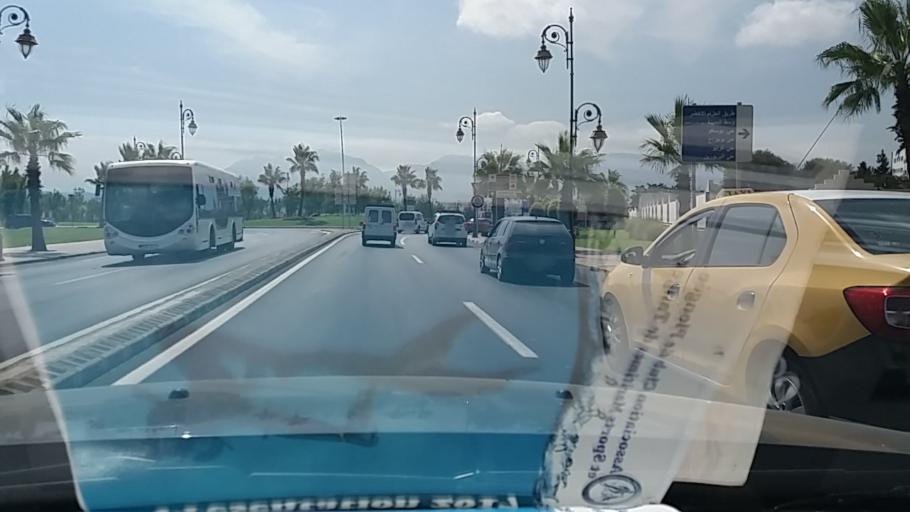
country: MA
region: Tanger-Tetouan
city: Tetouan
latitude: 35.6012
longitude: -5.3366
